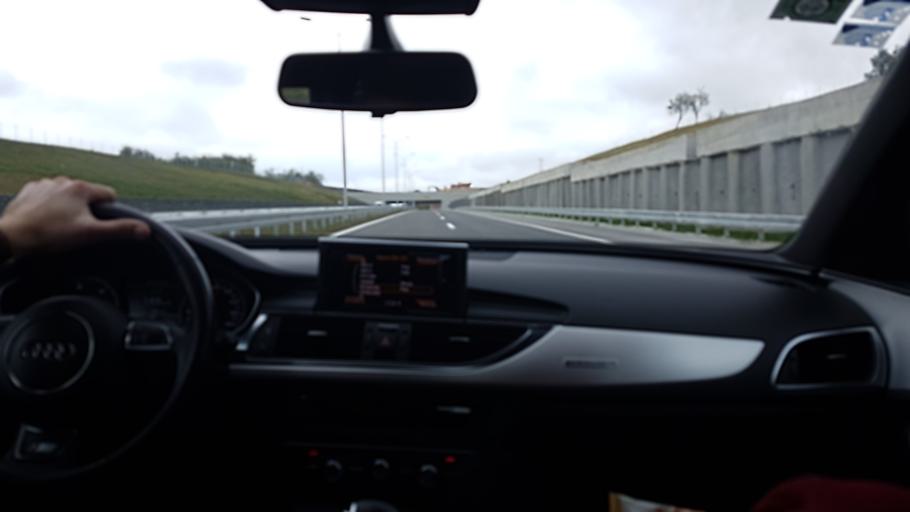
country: BA
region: Republika Srpska
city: Prnjavor
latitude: 44.8513
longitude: 17.7281
